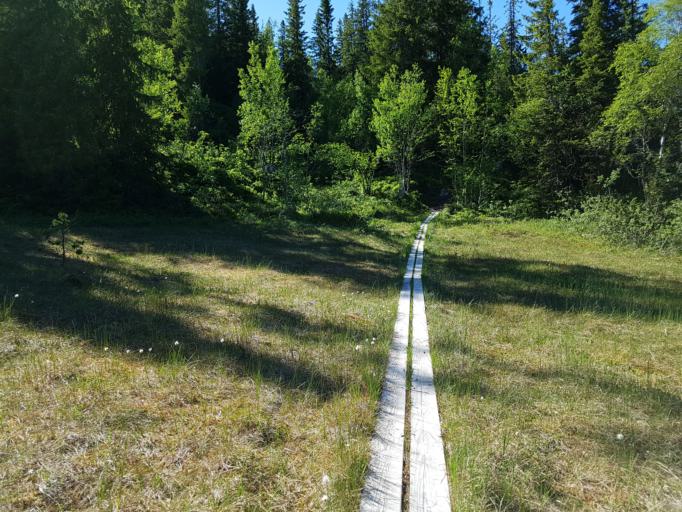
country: NO
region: Sor-Trondelag
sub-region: Trondheim
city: Trondheim
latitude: 63.4301
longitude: 10.2926
